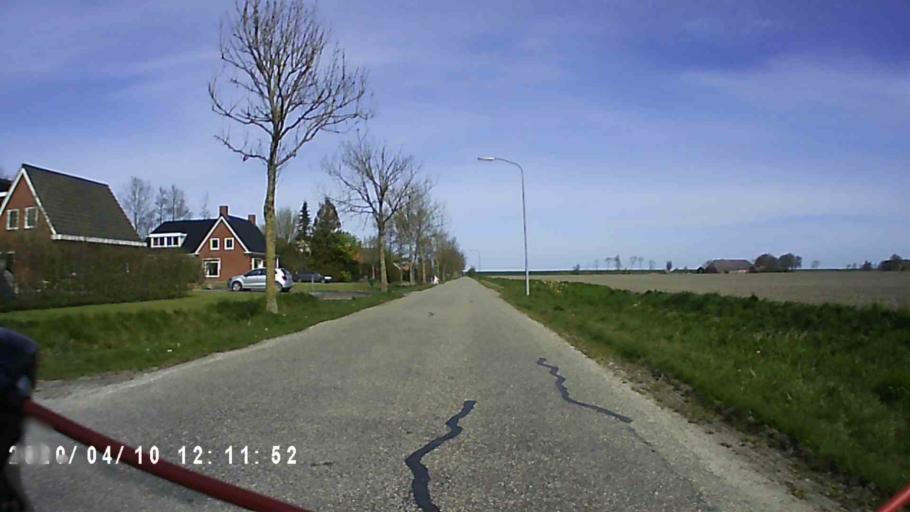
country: NL
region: Groningen
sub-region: Gemeente De Marne
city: Ulrum
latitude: 53.3905
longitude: 6.3742
